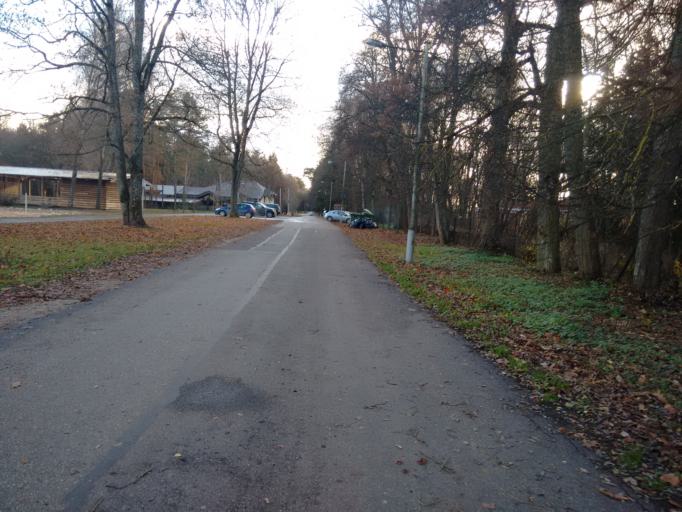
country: LT
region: Vilnius County
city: Vilkpede
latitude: 54.6839
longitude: 25.2341
